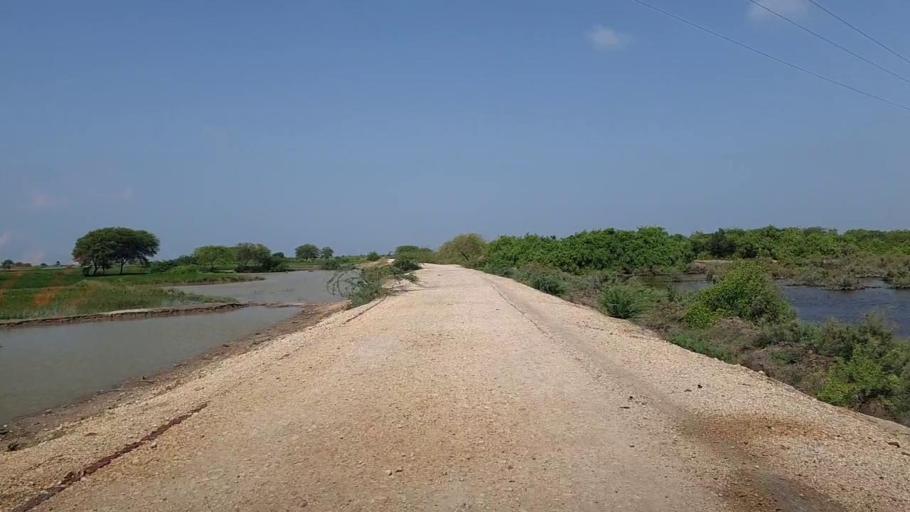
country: PK
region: Sindh
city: Mirpur Batoro
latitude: 24.6473
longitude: 68.4288
